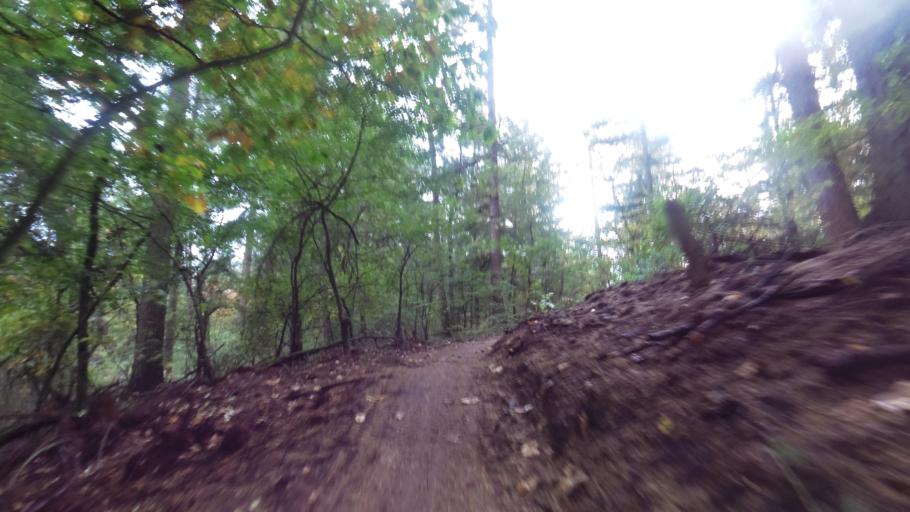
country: NL
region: Gelderland
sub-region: Gemeente Ede
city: Wekerom
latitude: 52.0859
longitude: 5.7255
